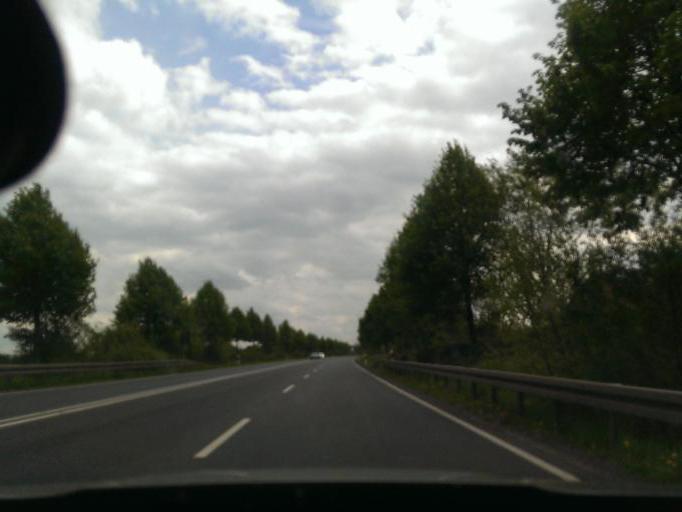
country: DE
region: Lower Saxony
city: Pattensen
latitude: 52.2669
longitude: 9.7800
